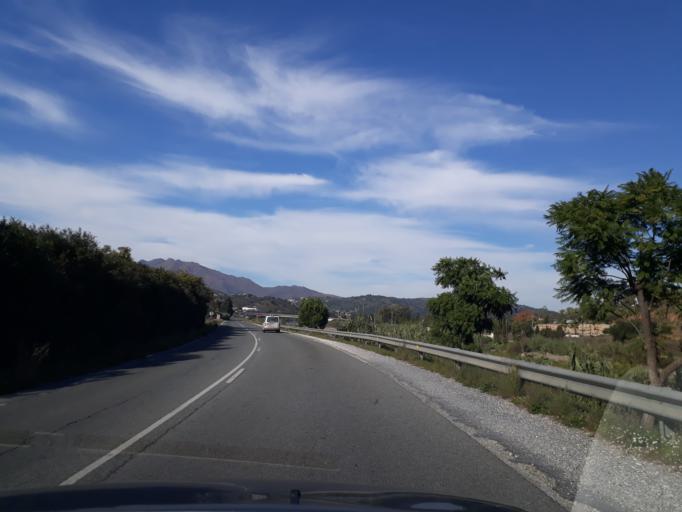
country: ES
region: Andalusia
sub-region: Provincia de Malaga
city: Fuengirola
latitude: 36.5465
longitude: -4.6893
